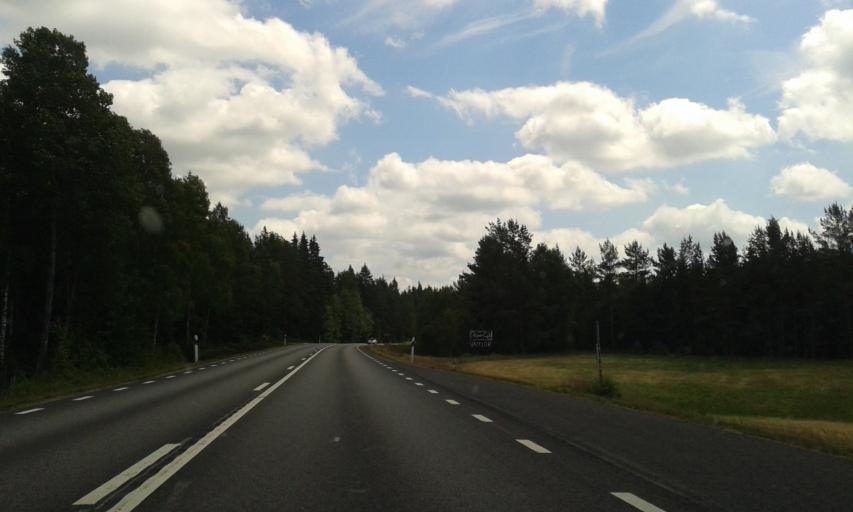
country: SE
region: Joenkoeping
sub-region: Varnamo Kommun
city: Rydaholm
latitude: 56.9265
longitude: 14.4106
